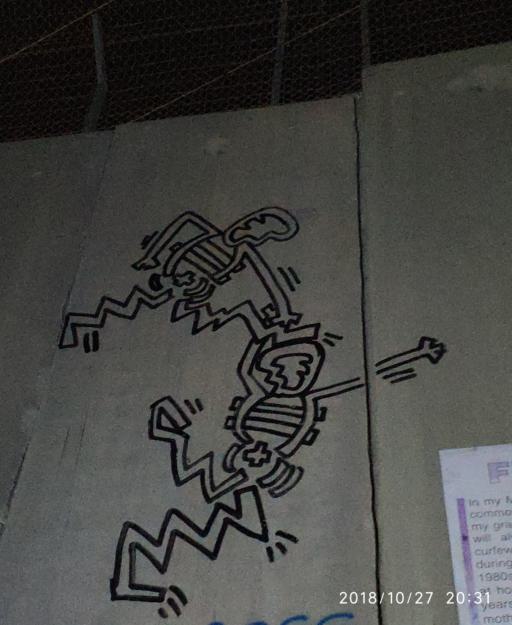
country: PS
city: Khallat Hamamah
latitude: 31.7197
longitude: 35.2027
